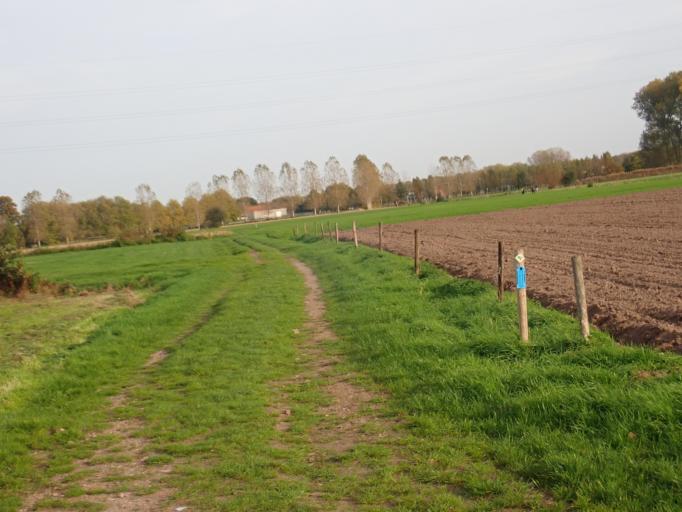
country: BE
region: Flanders
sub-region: Provincie Oost-Vlaanderen
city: Sint-Niklaas
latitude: 51.1630
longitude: 4.1022
